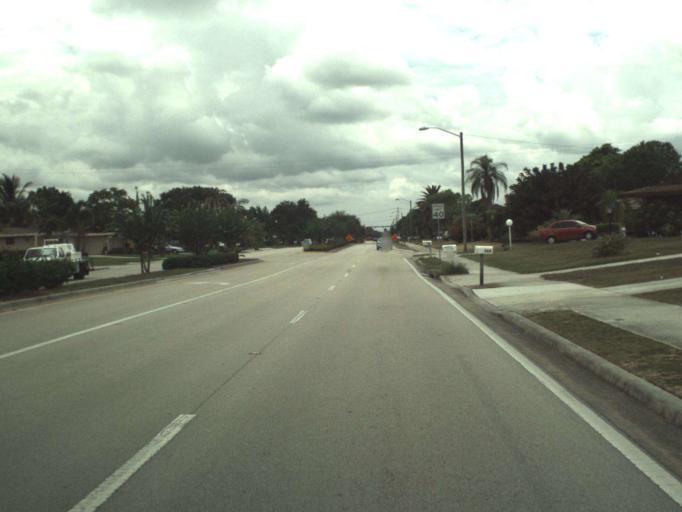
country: US
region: Florida
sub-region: Saint Lucie County
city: River Park
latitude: 27.3122
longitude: -80.3497
